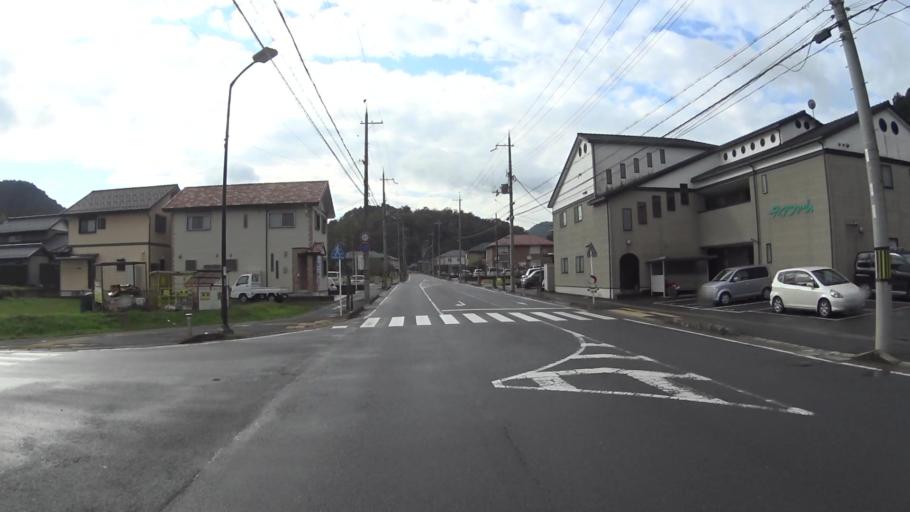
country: JP
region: Kyoto
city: Ayabe
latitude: 35.2983
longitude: 135.2348
